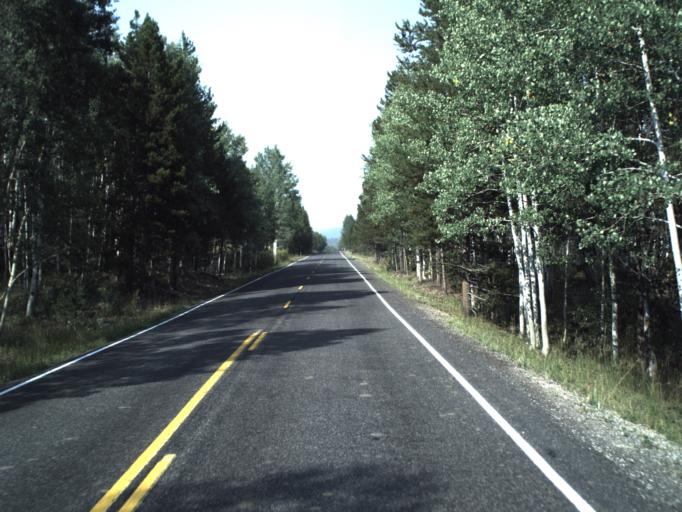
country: US
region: Wyoming
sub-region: Uinta County
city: Evanston
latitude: 40.8334
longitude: -110.8515
